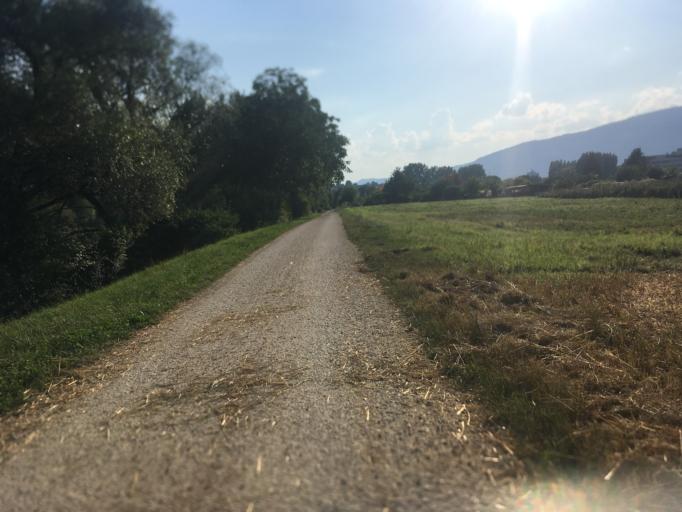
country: CH
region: Bern
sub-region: Biel/Bienne District
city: Brugg
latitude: 47.1177
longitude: 7.2715
